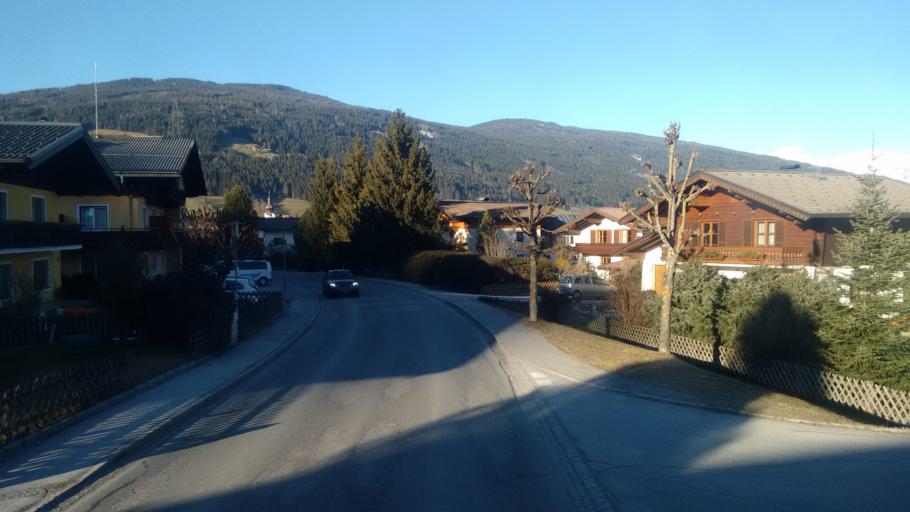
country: AT
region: Salzburg
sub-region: Politischer Bezirk Sankt Johann im Pongau
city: Altenmarkt im Pongau
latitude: 47.3722
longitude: 13.4209
